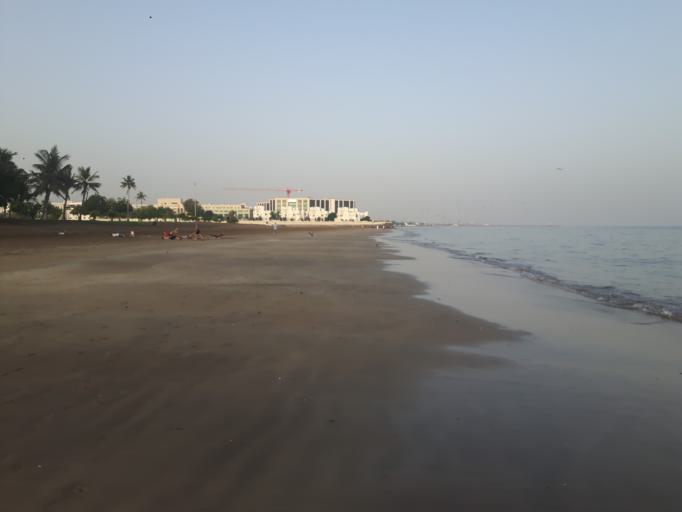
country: OM
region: Muhafazat Masqat
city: Bawshar
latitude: 23.6153
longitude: 58.4579
